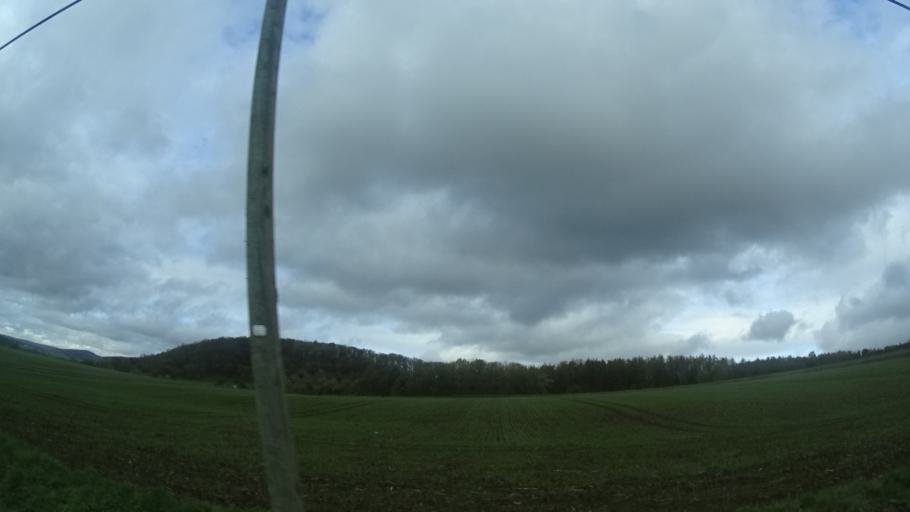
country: DE
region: Thuringia
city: Romhild
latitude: 50.4031
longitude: 10.5702
